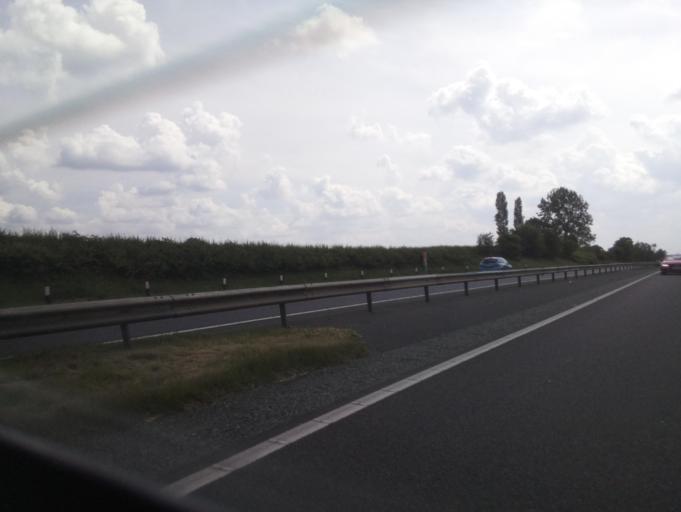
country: GB
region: England
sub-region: North Yorkshire
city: Thirsk
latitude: 54.3014
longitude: -1.3368
